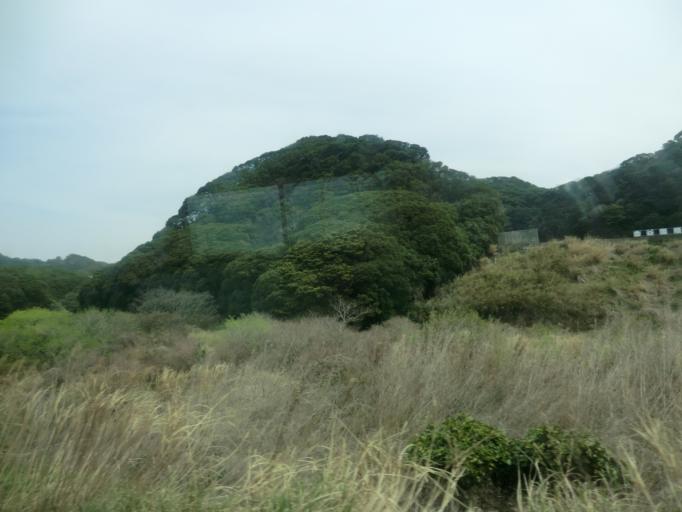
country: JP
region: Chiba
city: Futtsu
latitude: 35.1815
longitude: 139.8195
